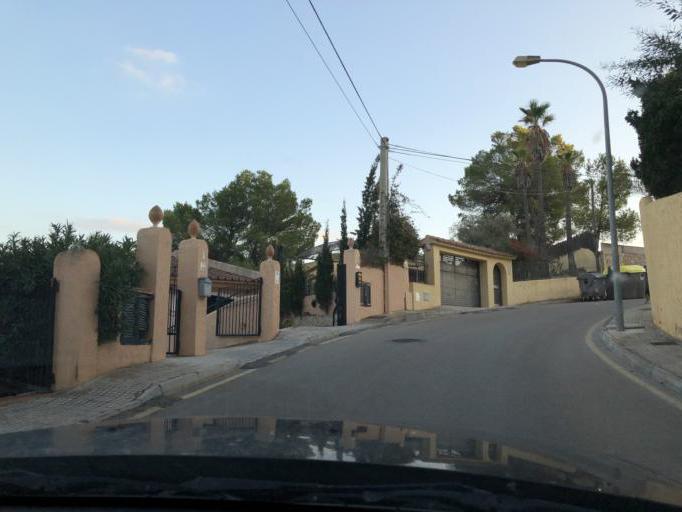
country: ES
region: Balearic Islands
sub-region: Illes Balears
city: Santa Ponsa
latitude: 39.5286
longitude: 2.4752
